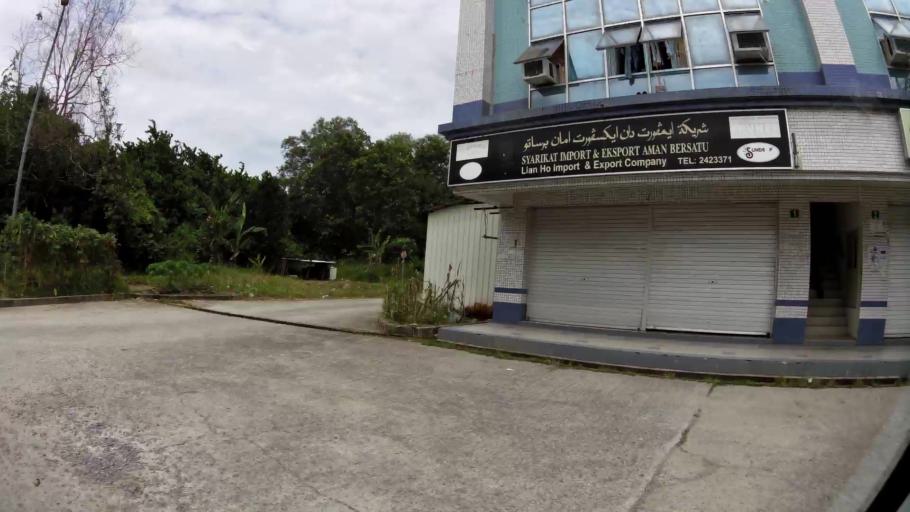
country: BN
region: Brunei and Muara
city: Bandar Seri Begawan
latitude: 4.9220
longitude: 114.9165
